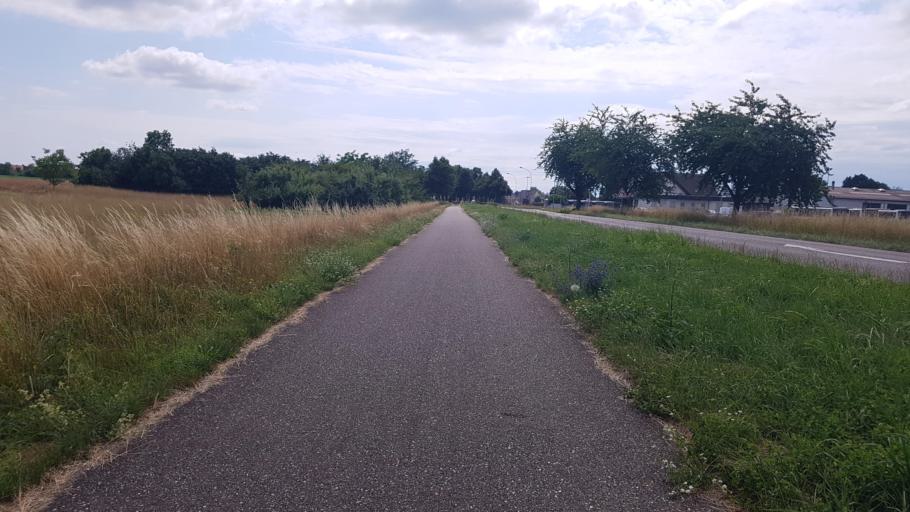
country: FR
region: Alsace
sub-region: Departement du Bas-Rhin
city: Herrlisheim
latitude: 48.7394
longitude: 7.9150
